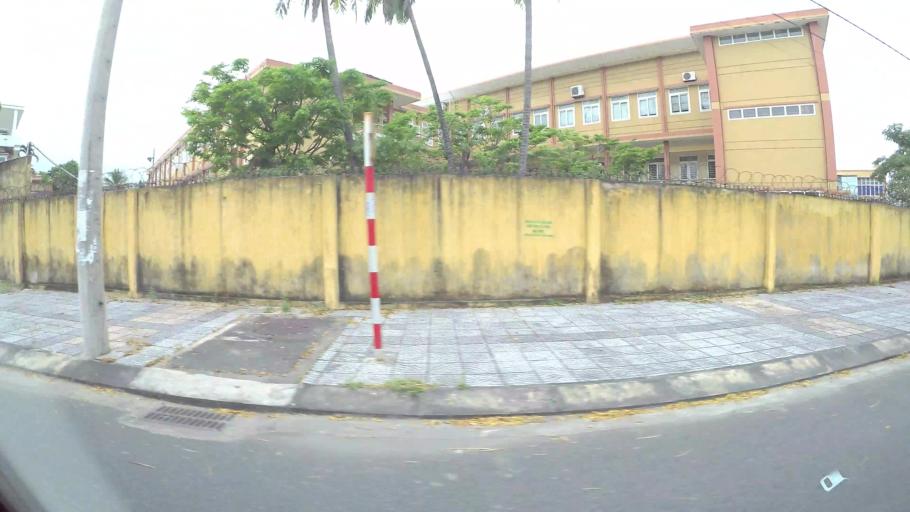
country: VN
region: Da Nang
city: Thanh Khe
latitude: 16.0701
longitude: 108.1821
